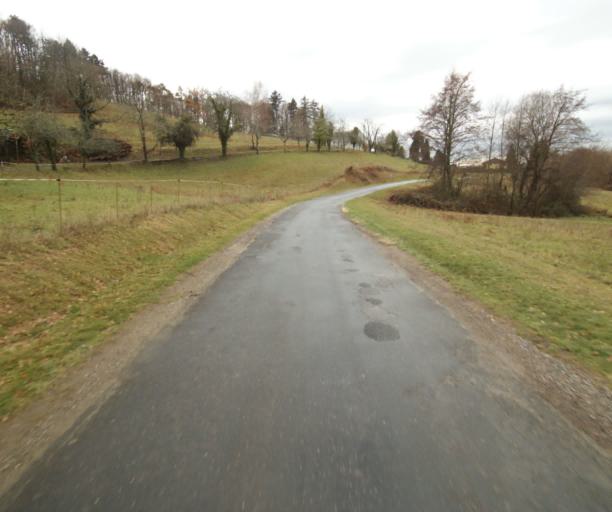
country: FR
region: Limousin
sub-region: Departement de la Correze
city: Saint-Mexant
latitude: 45.2836
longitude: 1.6443
